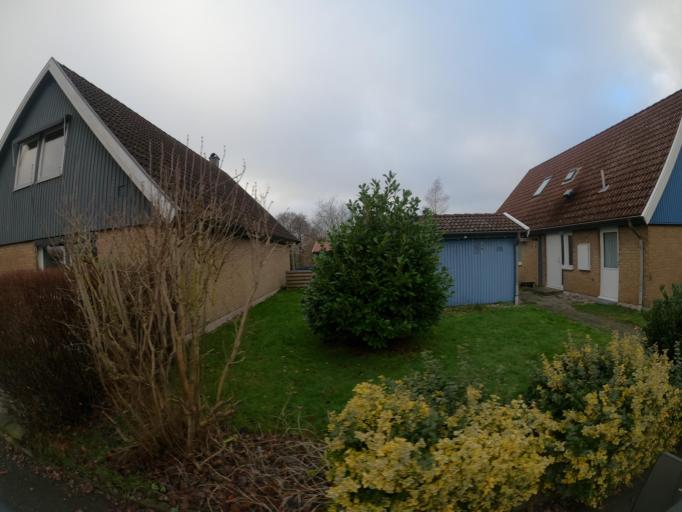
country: SE
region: Skane
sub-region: Svedala Kommun
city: Svedala
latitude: 55.5242
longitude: 13.2112
